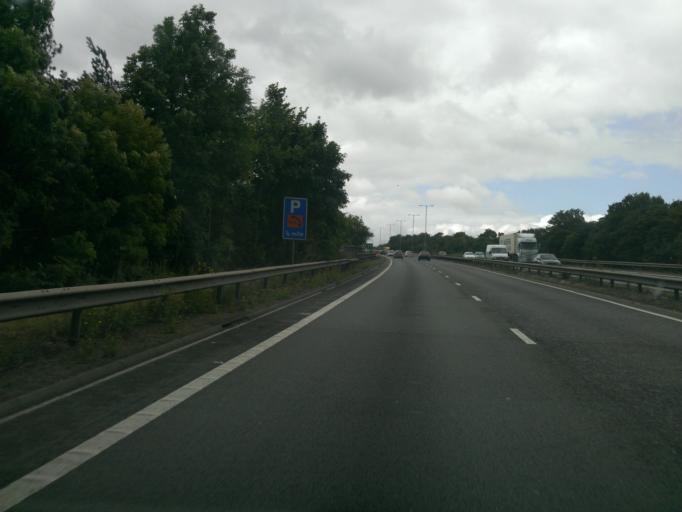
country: GB
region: England
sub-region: Essex
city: West Bergholt
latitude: 51.8961
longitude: 0.8568
